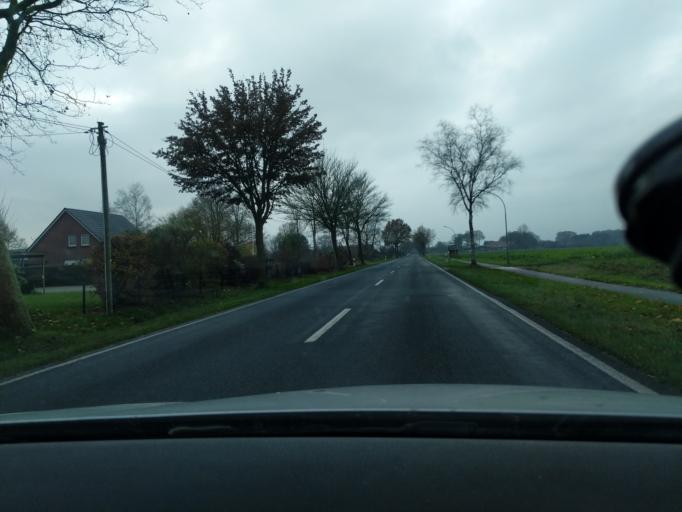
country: DE
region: Lower Saxony
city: Ahlerstedt
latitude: 53.3868
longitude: 9.4771
